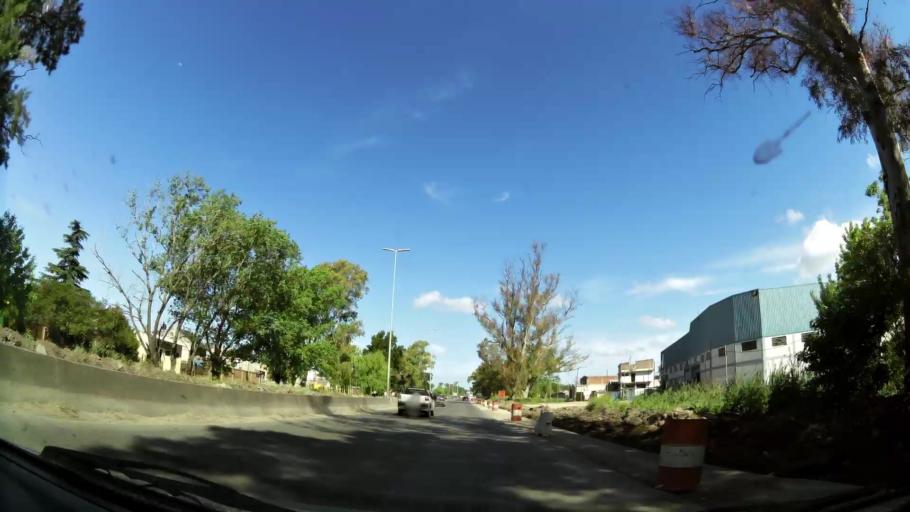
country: AR
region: Buenos Aires
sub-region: Partido de Quilmes
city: Quilmes
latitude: -34.7979
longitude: -58.2421
